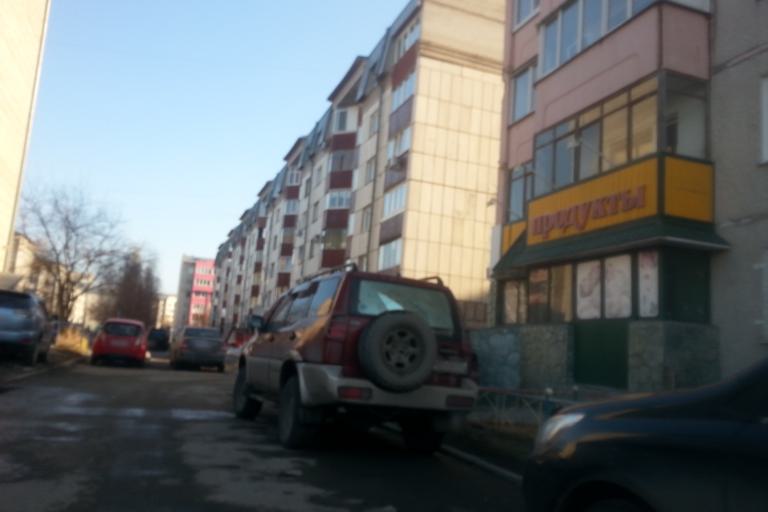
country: RU
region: Altai Krai
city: Novosilikatnyy
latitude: 53.3311
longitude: 83.6728
